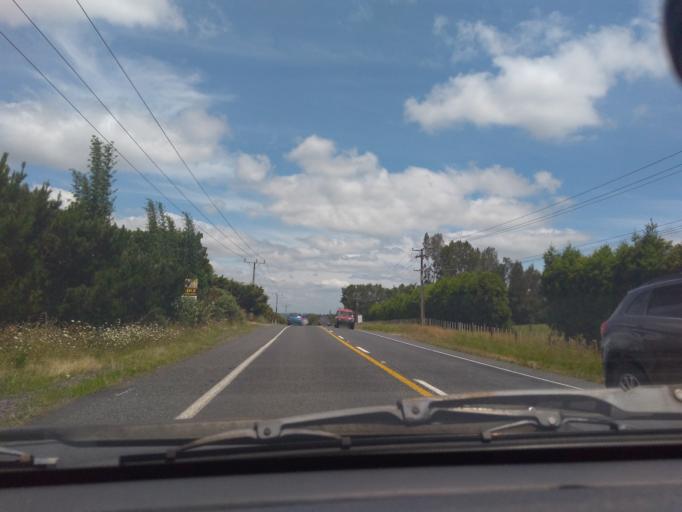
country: NZ
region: Northland
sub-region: Far North District
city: Kerikeri
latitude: -35.1601
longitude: 173.8912
